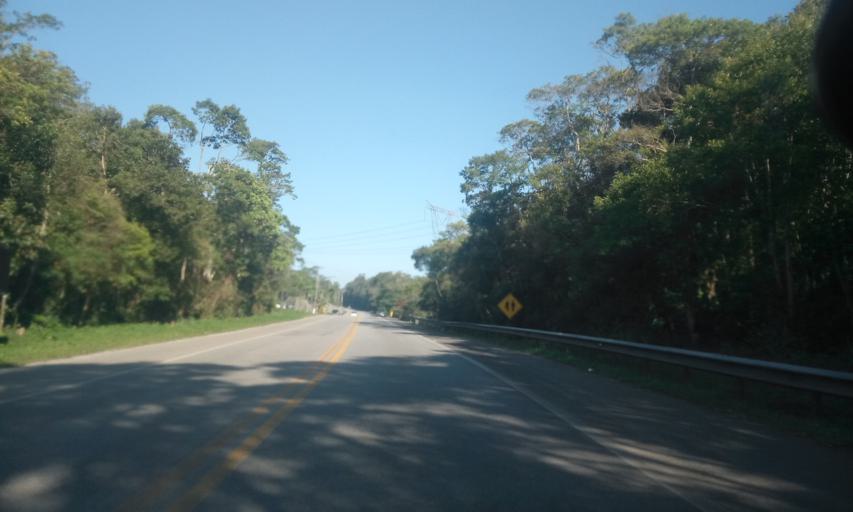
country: BR
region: Sao Paulo
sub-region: Cubatao
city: Cubatao
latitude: -23.8077
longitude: -46.4912
